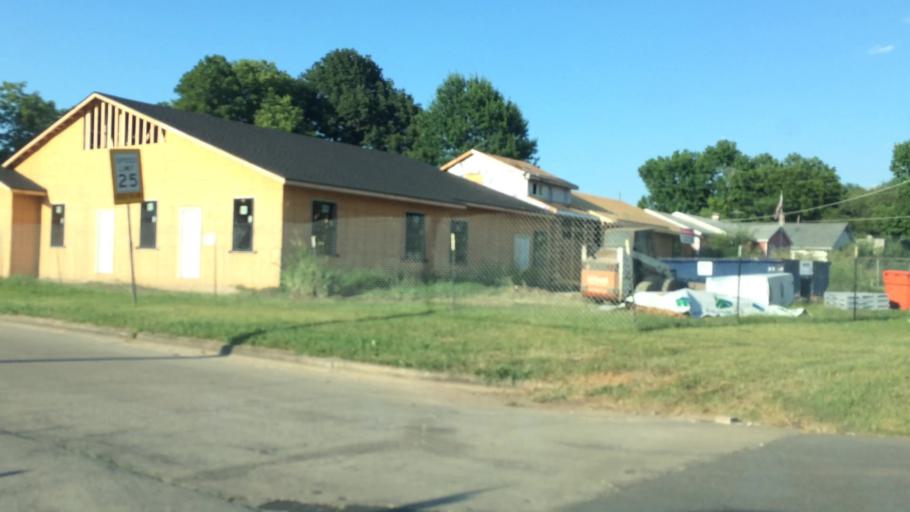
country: US
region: Missouri
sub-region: Greene County
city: Springfield
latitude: 37.1961
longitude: -93.2573
